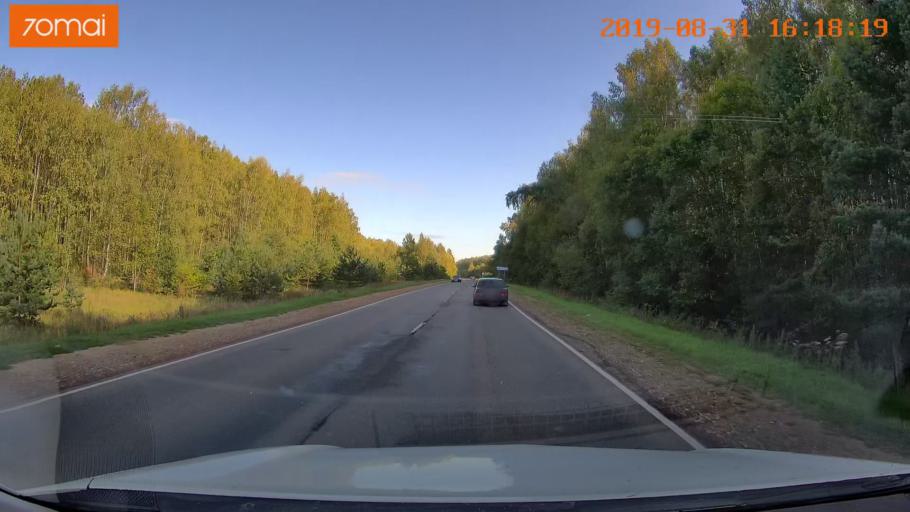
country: RU
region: Kaluga
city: Nikola-Lenivets
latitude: 54.5375
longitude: 35.5525
